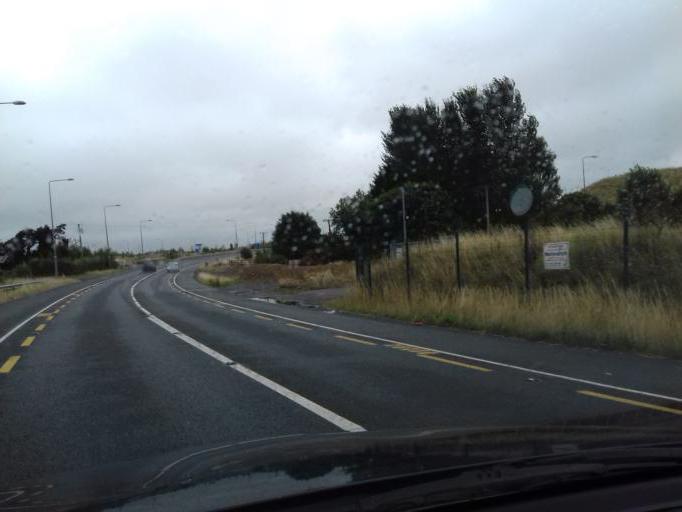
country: IE
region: Leinster
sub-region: County Carlow
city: Bagenalstown
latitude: 52.7663
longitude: -6.9562
